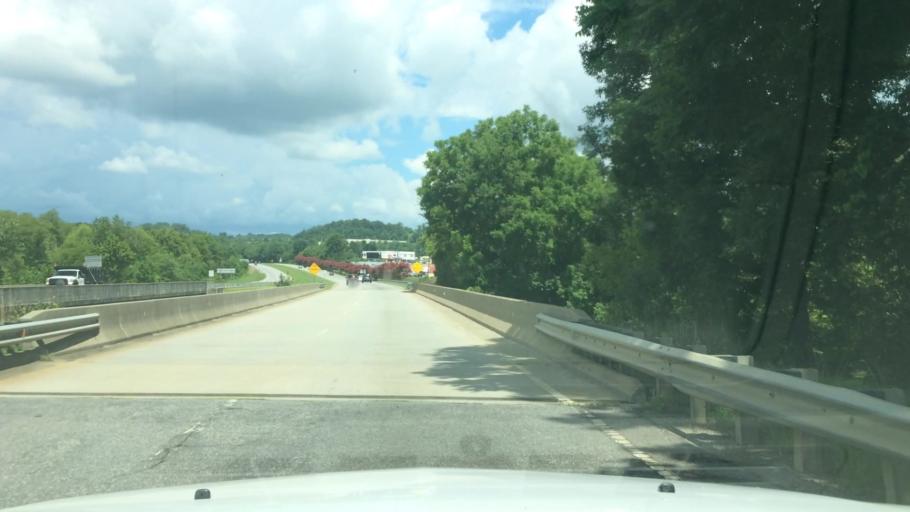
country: US
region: North Carolina
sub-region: Wilkes County
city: Wilkesboro
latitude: 36.1450
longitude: -81.1770
